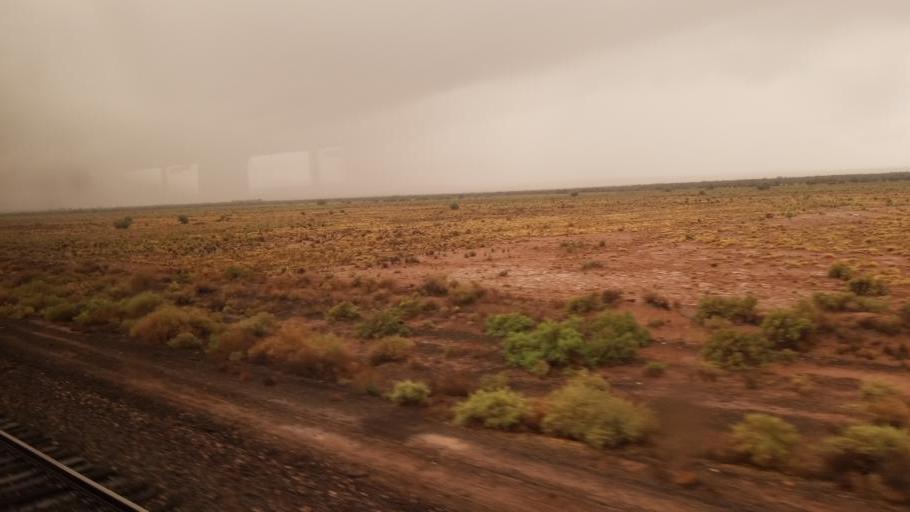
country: US
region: Arizona
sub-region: Navajo County
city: Joseph City
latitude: 34.9675
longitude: -110.4928
